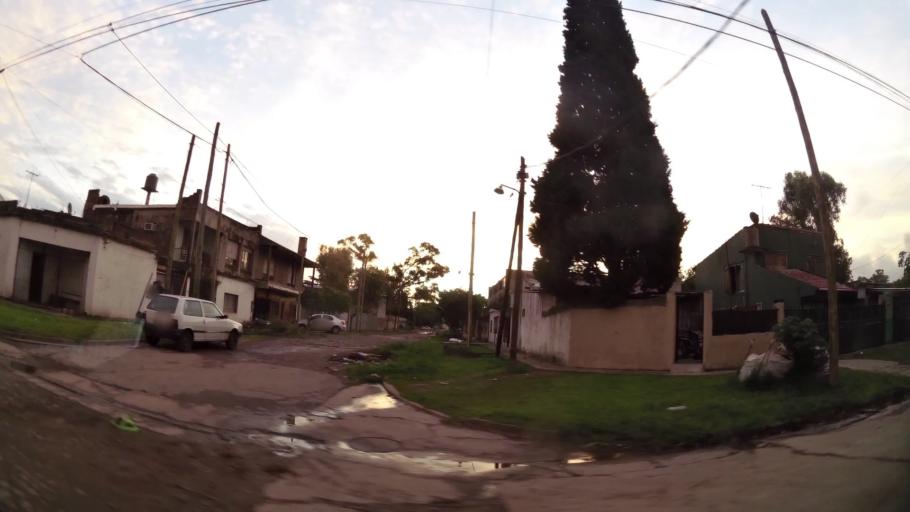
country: AR
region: Buenos Aires
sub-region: Partido de Lomas de Zamora
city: Lomas de Zamora
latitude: -34.7557
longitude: -58.3643
